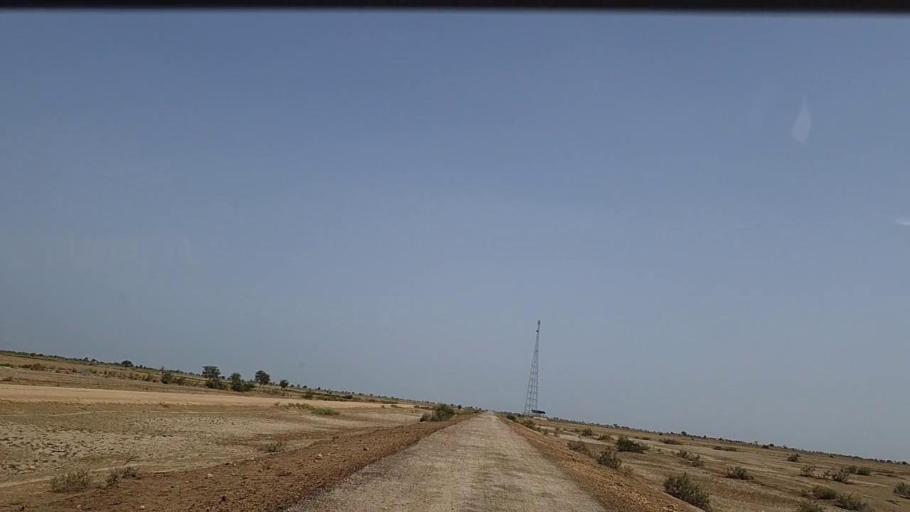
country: PK
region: Sindh
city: Phulji
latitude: 26.7928
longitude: 67.6411
